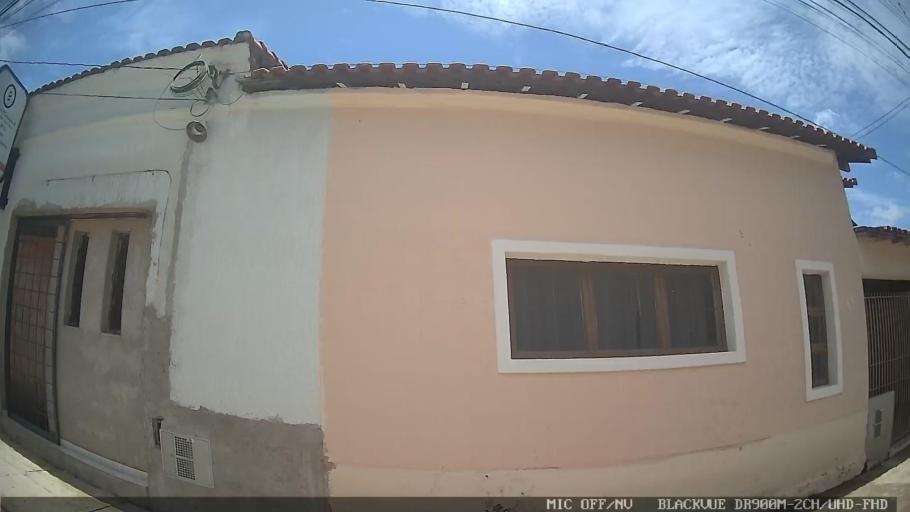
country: BR
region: Sao Paulo
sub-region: Laranjal Paulista
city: Laranjal Paulista
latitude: -23.0507
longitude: -47.8345
